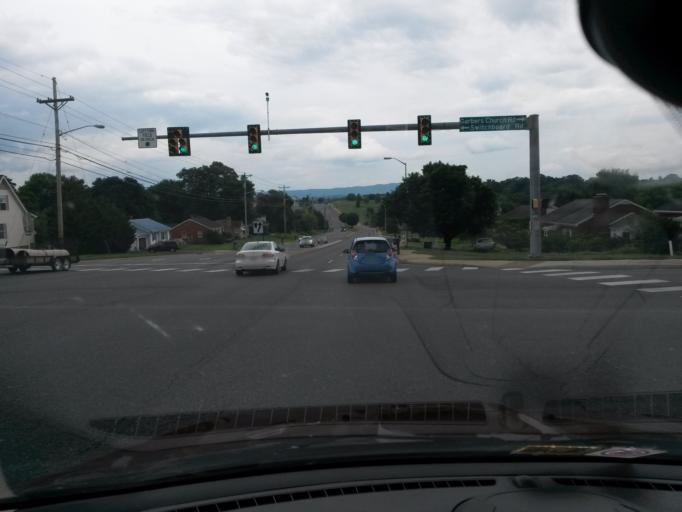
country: US
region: Virginia
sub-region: City of Harrisonburg
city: Harrisonburg
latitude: 38.4554
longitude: -78.8994
